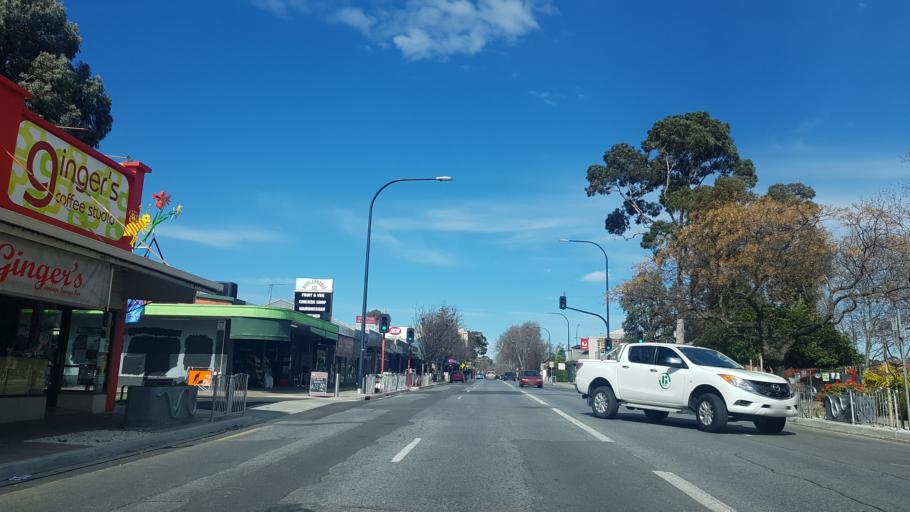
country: AU
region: South Australia
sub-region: Unley
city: Millswood
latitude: -34.9510
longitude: 138.5897
